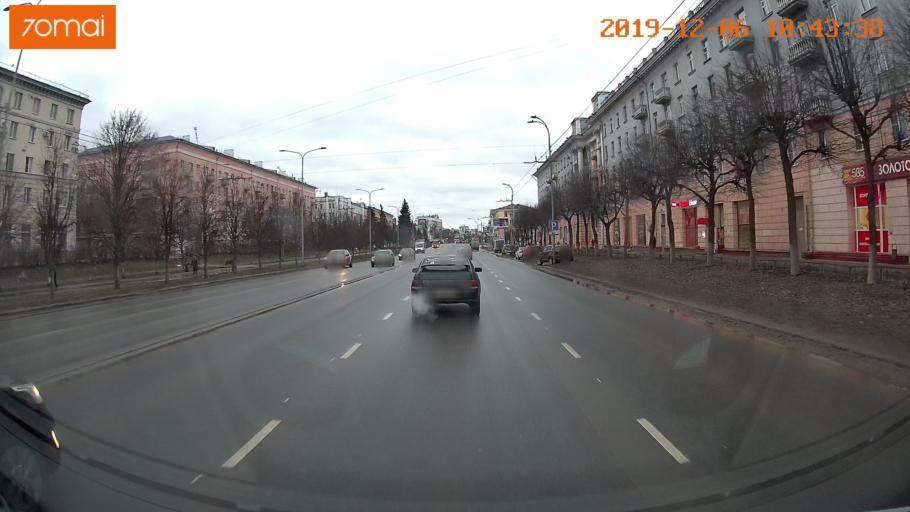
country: RU
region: Ivanovo
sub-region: Gorod Ivanovo
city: Ivanovo
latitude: 57.0136
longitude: 40.9706
